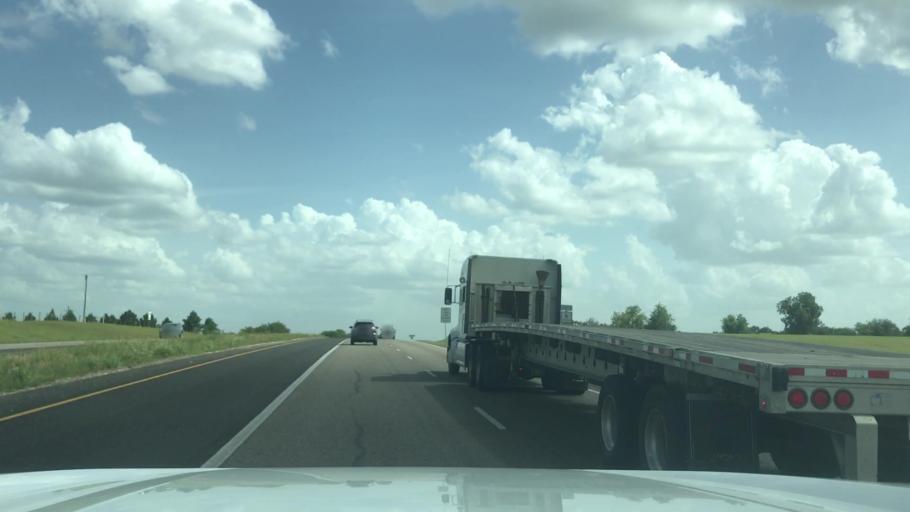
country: US
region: Texas
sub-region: Grimes County
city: Navasota
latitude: 30.3083
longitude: -96.0468
